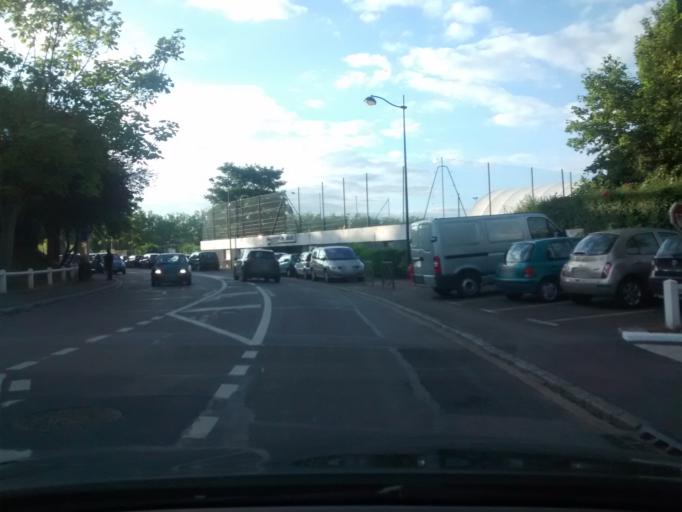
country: FR
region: Ile-de-France
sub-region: Departement des Yvelines
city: Le Chesnay
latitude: 48.8188
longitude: 2.1211
